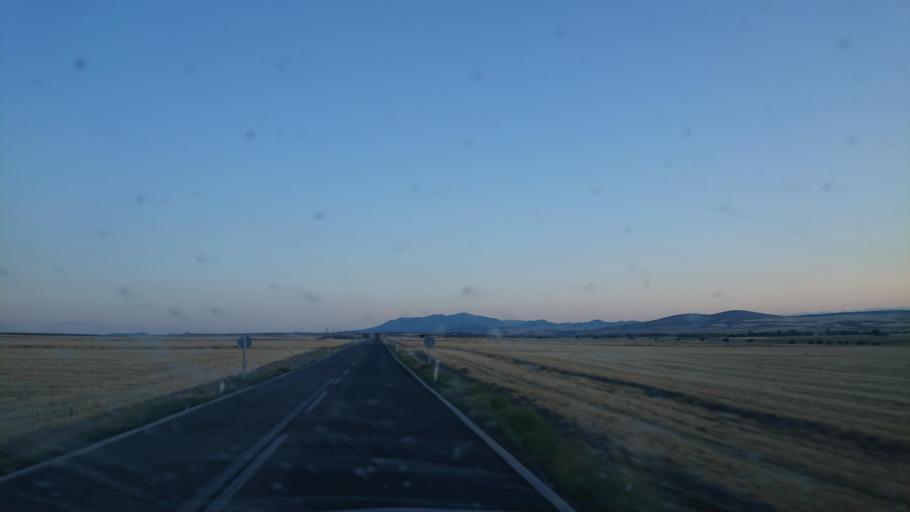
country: TR
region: Aksaray
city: Balci
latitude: 38.8305
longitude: 34.1388
